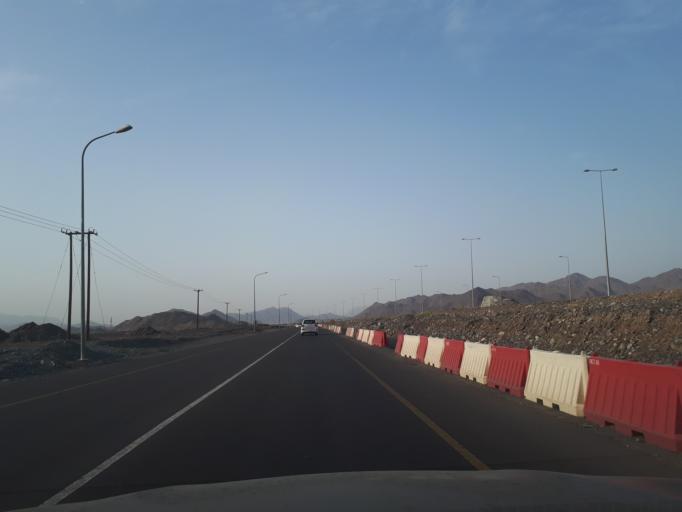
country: OM
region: Muhafazat ad Dakhiliyah
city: Sufalat Sama'il
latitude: 23.2752
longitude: 58.1058
